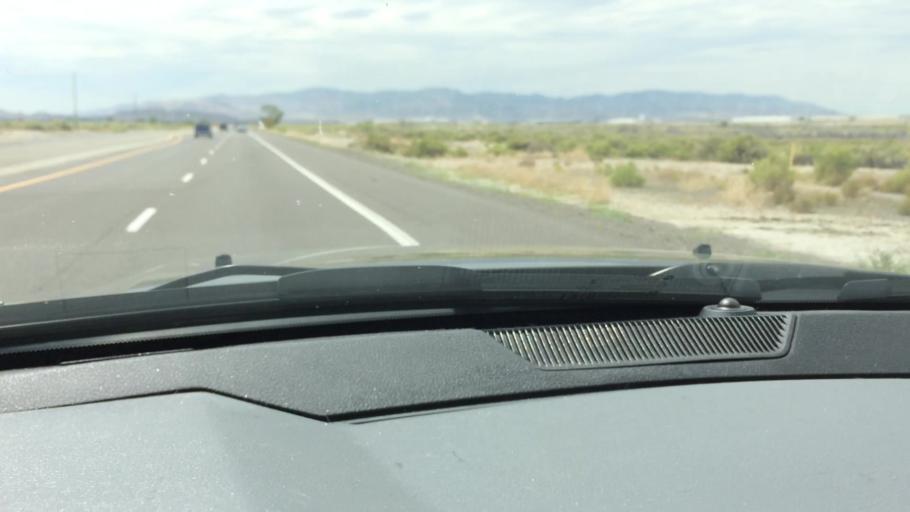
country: US
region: Nevada
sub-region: Lyon County
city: Fernley
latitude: 39.5956
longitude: -119.1757
